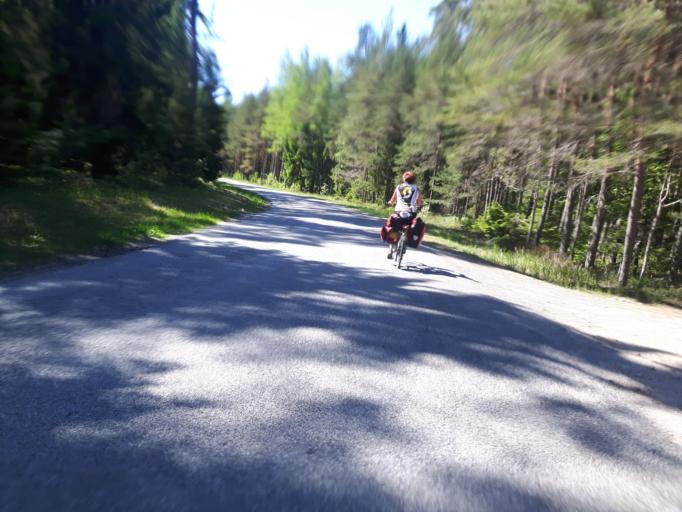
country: EE
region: Laeaene-Virumaa
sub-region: Haljala vald
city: Haljala
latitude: 59.5532
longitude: 26.3463
